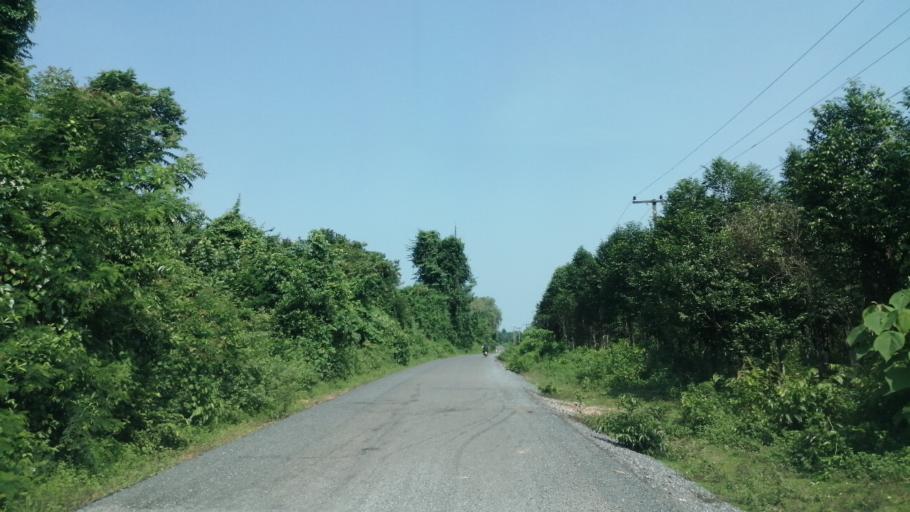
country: LA
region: Bolikhamxai
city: Bolikhan
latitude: 18.4550
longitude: 103.8033
